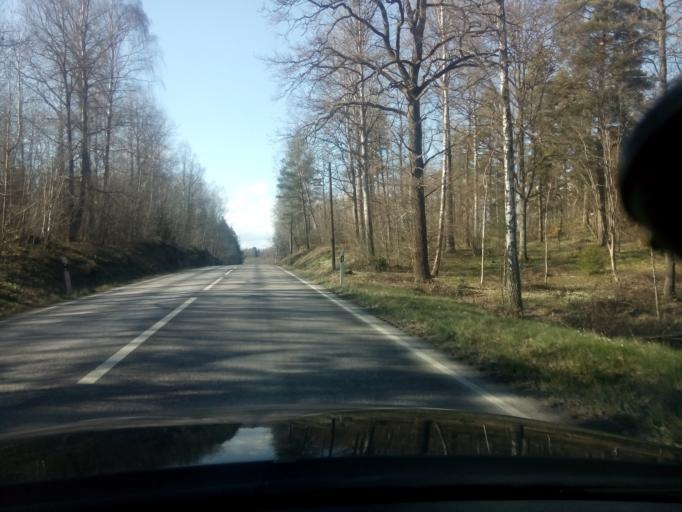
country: SE
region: Soedermanland
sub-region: Flens Kommun
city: Malmkoping
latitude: 59.0768
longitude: 16.8130
